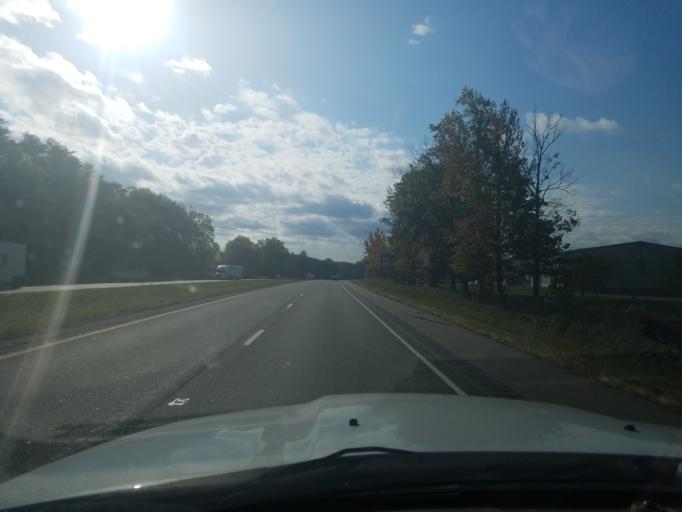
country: US
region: Indiana
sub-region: Scott County
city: Scottsburg
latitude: 38.7020
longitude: -85.7917
